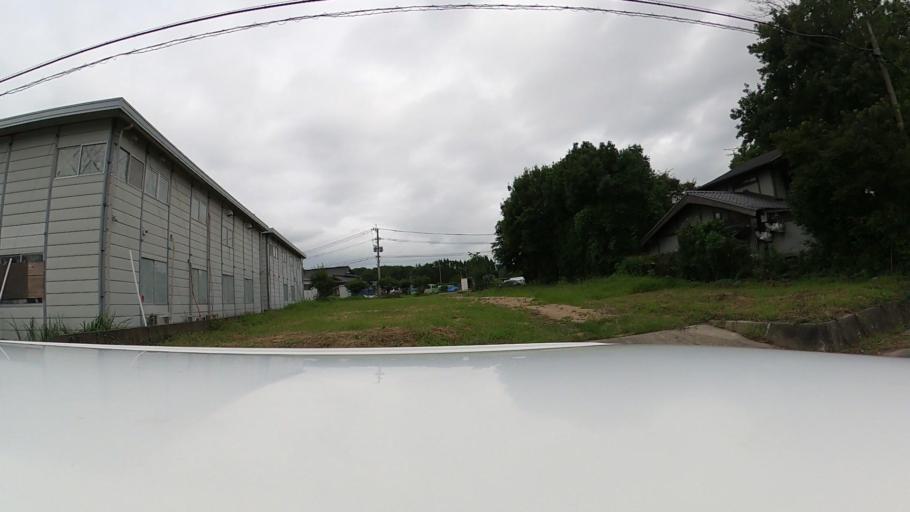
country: JP
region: Kumamoto
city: Ozu
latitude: 32.8357
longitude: 130.8739
